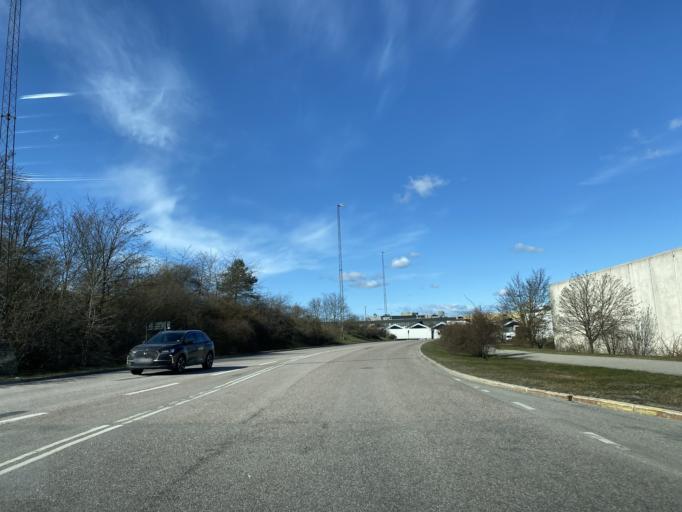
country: SE
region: Stockholm
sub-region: Stockholms Kommun
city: Arsta
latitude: 59.2921
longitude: 18.0362
